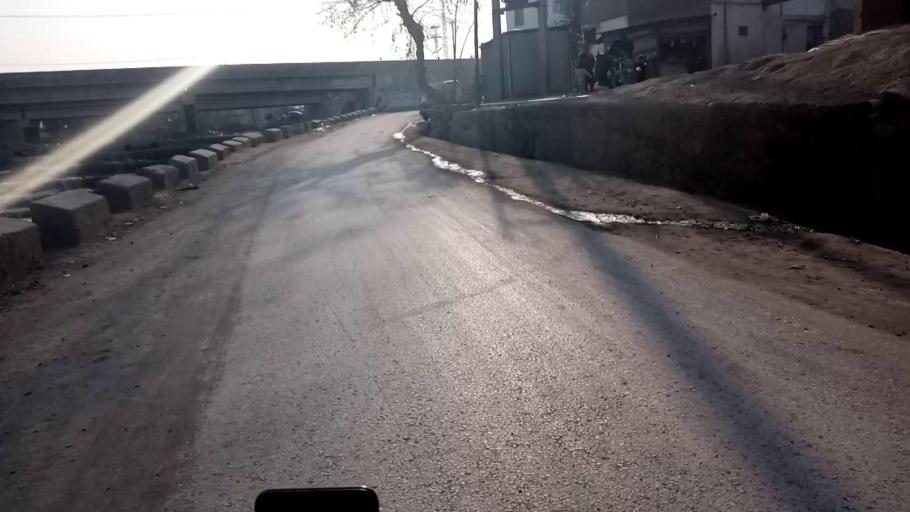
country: PK
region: Khyber Pakhtunkhwa
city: Peshawar
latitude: 34.0047
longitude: 71.4668
